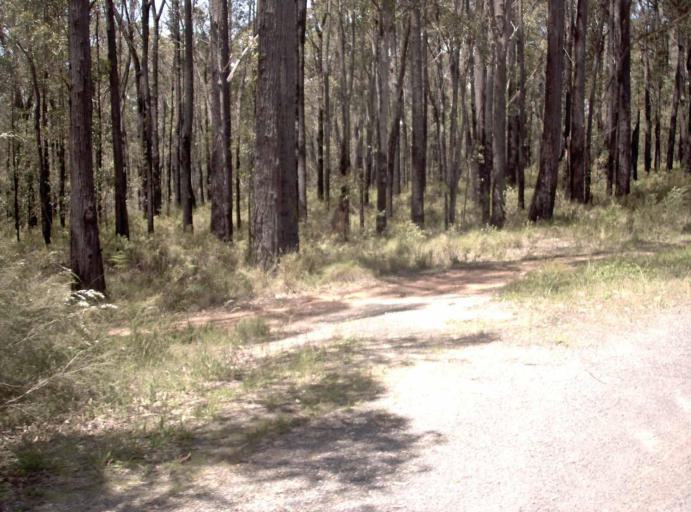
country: AU
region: Victoria
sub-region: East Gippsland
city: Lakes Entrance
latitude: -37.6918
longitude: 148.6279
